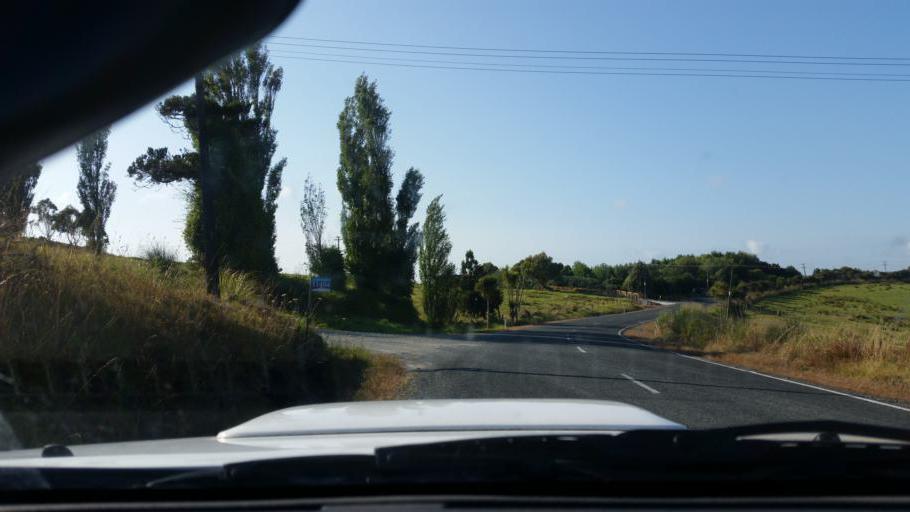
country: NZ
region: Northland
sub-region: Whangarei
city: Ruakaka
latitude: -36.1218
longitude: 174.2329
